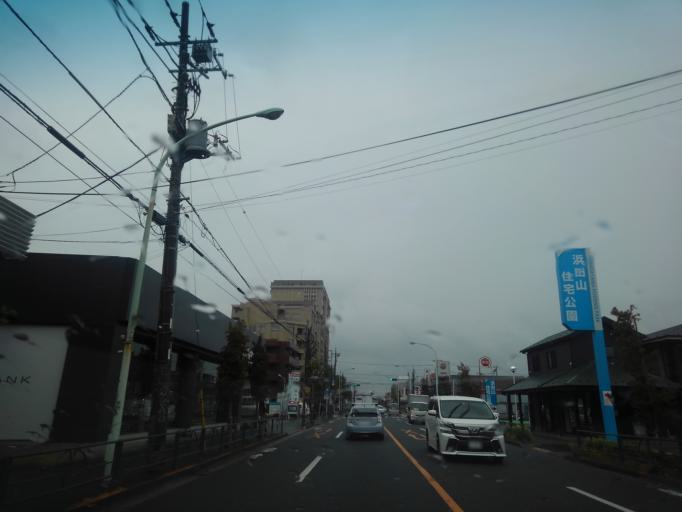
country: JP
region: Tokyo
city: Mitaka-shi
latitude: 35.6860
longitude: 139.6236
